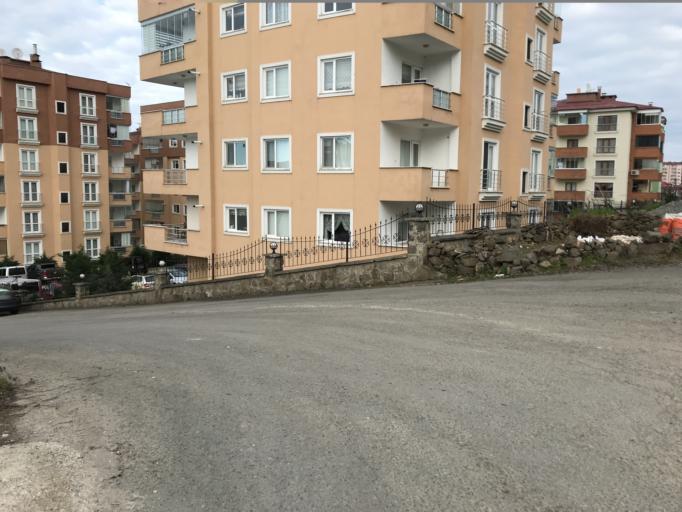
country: TR
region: Trabzon
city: Trabzon
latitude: 40.9899
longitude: 39.7800
